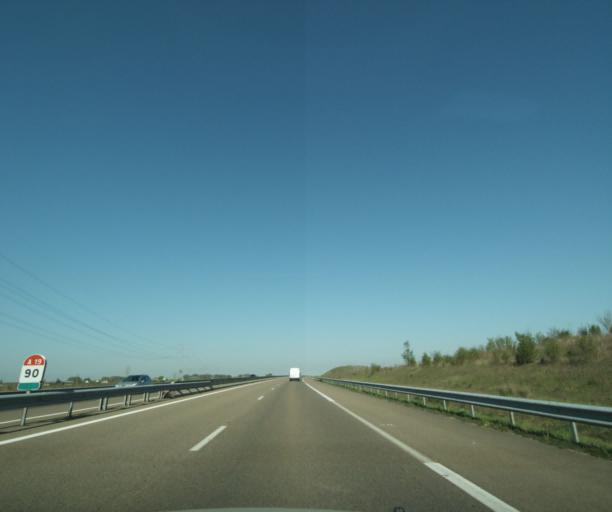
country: FR
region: Centre
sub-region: Departement du Loiret
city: Boynes
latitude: 48.1021
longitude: 2.3347
